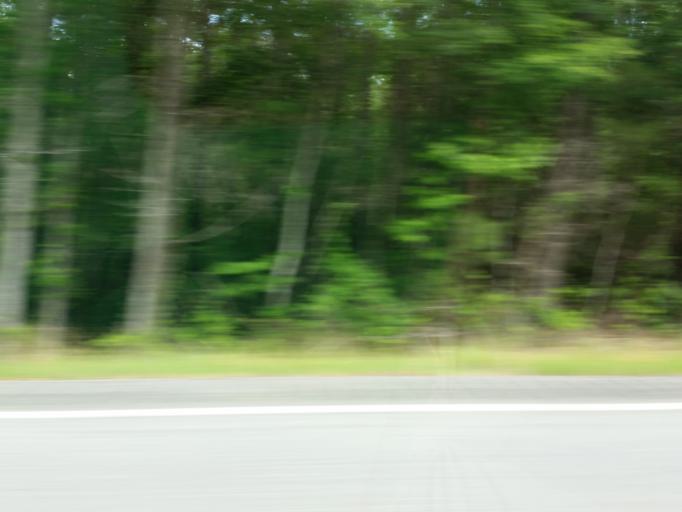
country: US
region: Alabama
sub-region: Sumter County
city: York
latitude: 32.3791
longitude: -88.1967
